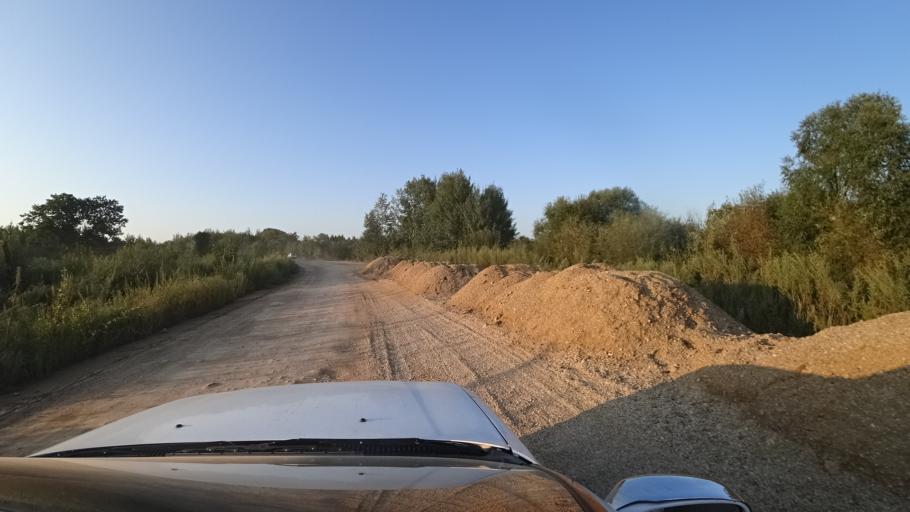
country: RU
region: Primorskiy
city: Dal'nerechensk
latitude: 45.9409
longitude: 133.7611
